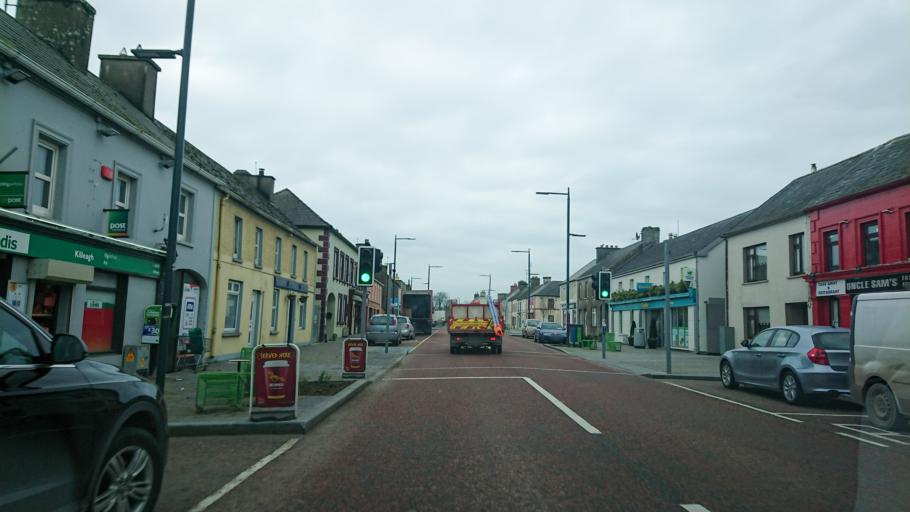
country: IE
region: Munster
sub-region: County Cork
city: Castlemartyr
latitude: 51.9418
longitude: -7.9933
